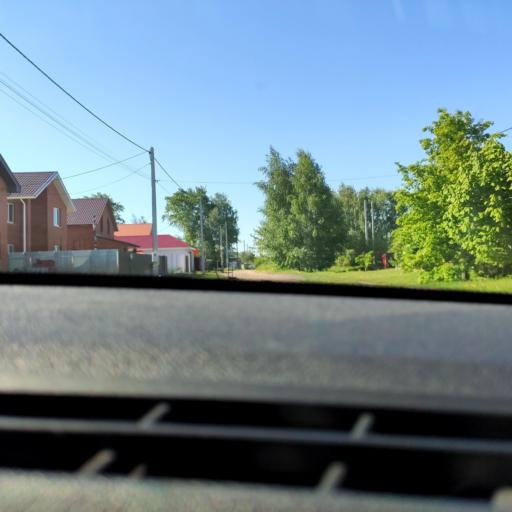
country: RU
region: Samara
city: Tol'yatti
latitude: 53.5594
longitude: 49.4098
